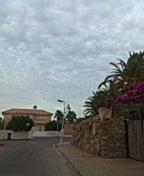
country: ES
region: Murcia
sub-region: Murcia
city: San Pedro del Pinatar
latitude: 37.7774
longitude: -0.7533
